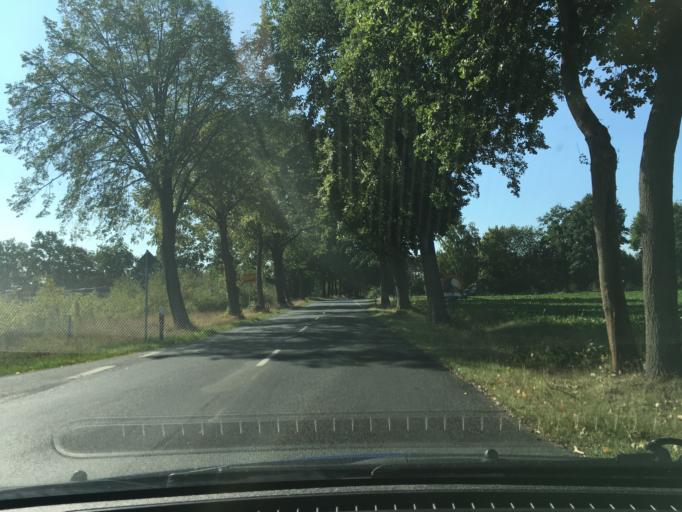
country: DE
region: Lower Saxony
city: Wriedel
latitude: 53.0266
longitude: 10.2829
